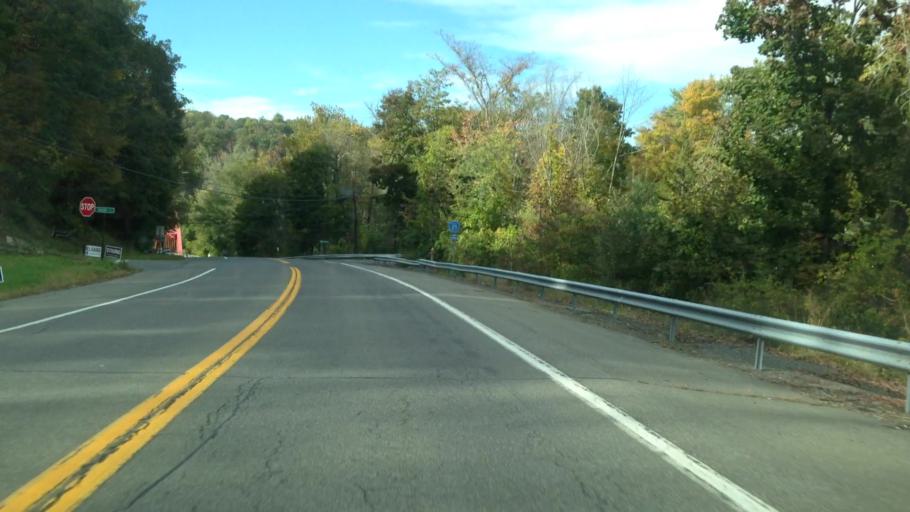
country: US
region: New York
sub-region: Ulster County
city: Kingston
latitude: 41.8926
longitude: -74.0168
